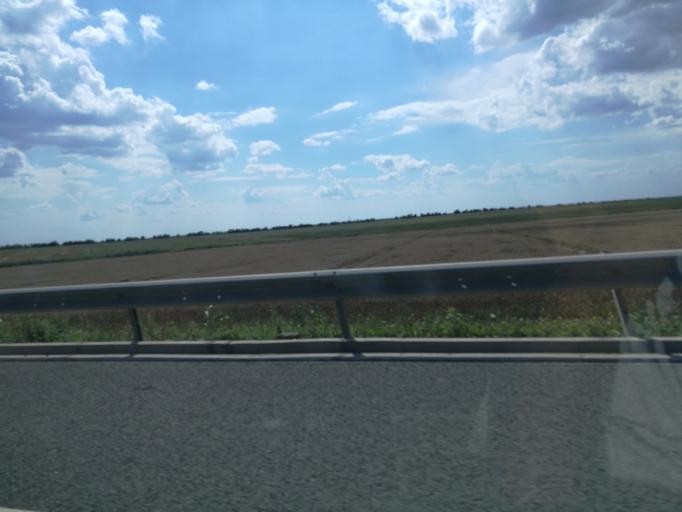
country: RO
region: Constanta
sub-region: Municipiul Constanta
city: Palazu Mare
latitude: 44.2043
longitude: 28.5525
